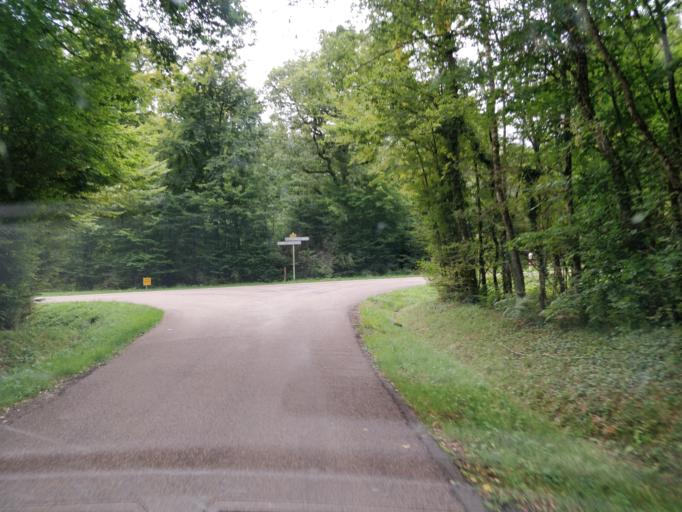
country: FR
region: Champagne-Ardenne
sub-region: Departement de l'Aube
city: Ervy-le-Chatel
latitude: 48.1374
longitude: 3.8719
